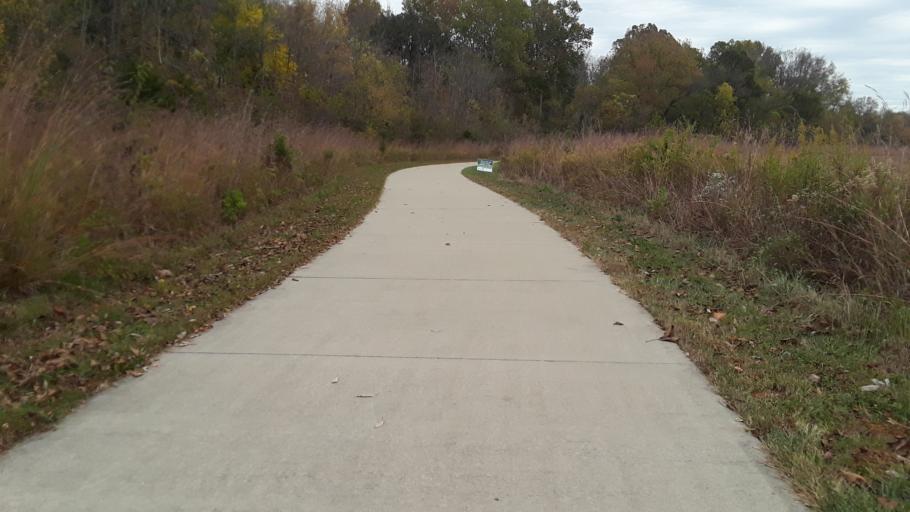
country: US
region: Kentucky
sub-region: Jefferson County
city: Middletown
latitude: 38.2044
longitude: -85.4770
